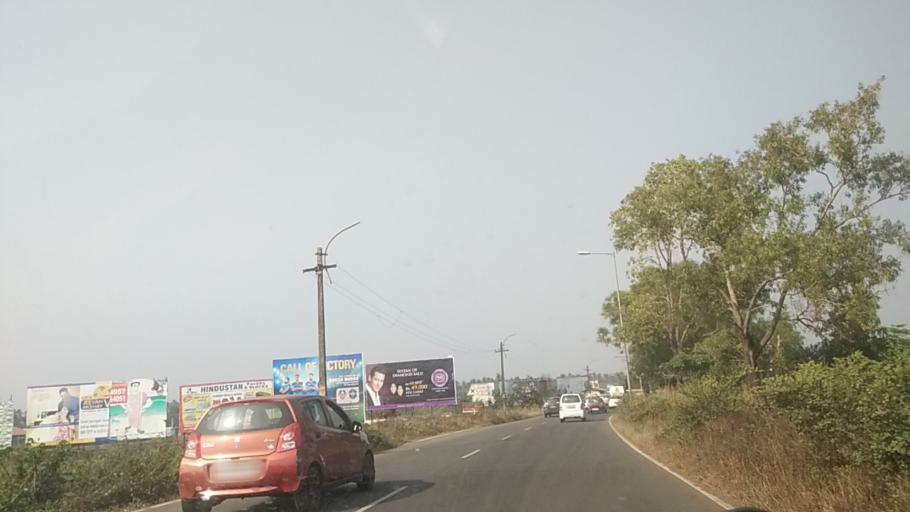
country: IN
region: Goa
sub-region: North Goa
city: Guirim
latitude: 15.5717
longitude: 73.8065
